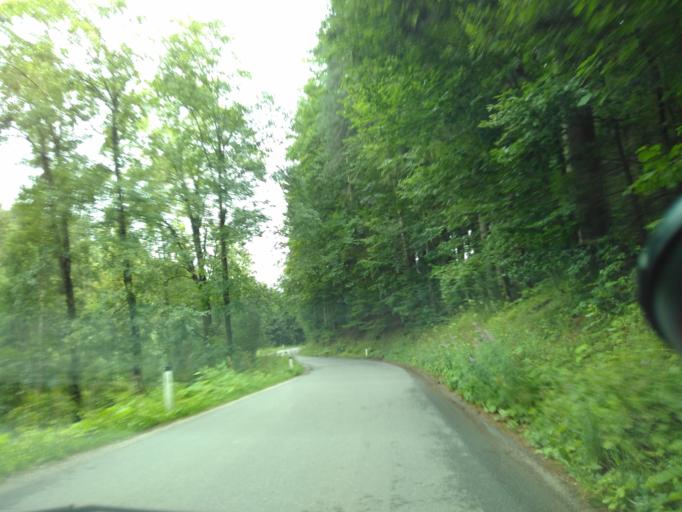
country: AT
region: Styria
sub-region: Politischer Bezirk Graz-Umgebung
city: Semriach
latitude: 47.2265
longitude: 15.3996
